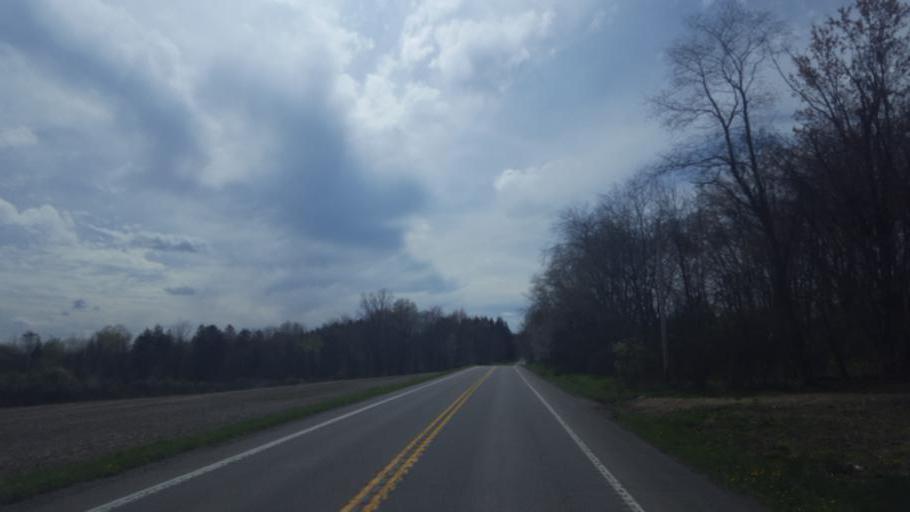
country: US
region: Pennsylvania
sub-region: Mercer County
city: Stoneboro
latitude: 41.3492
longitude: -80.0065
